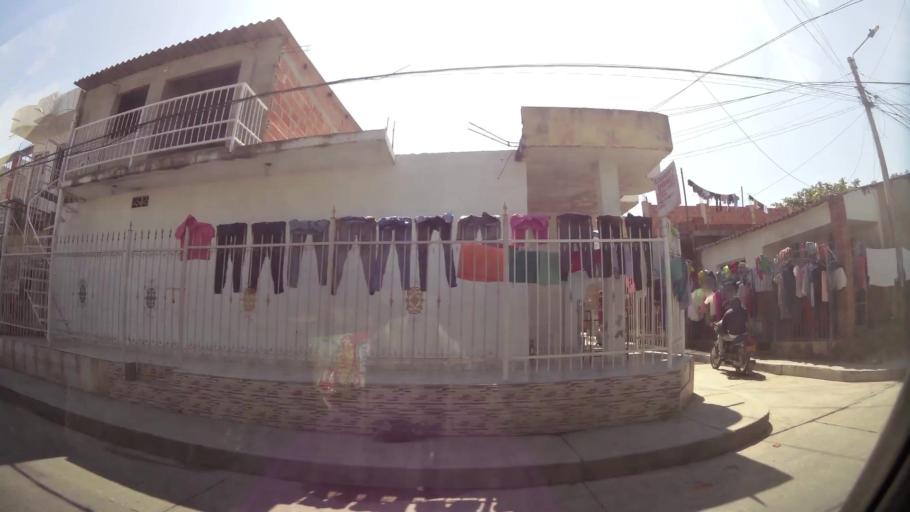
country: CO
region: Bolivar
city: Cartagena
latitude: 10.3881
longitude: -75.4552
